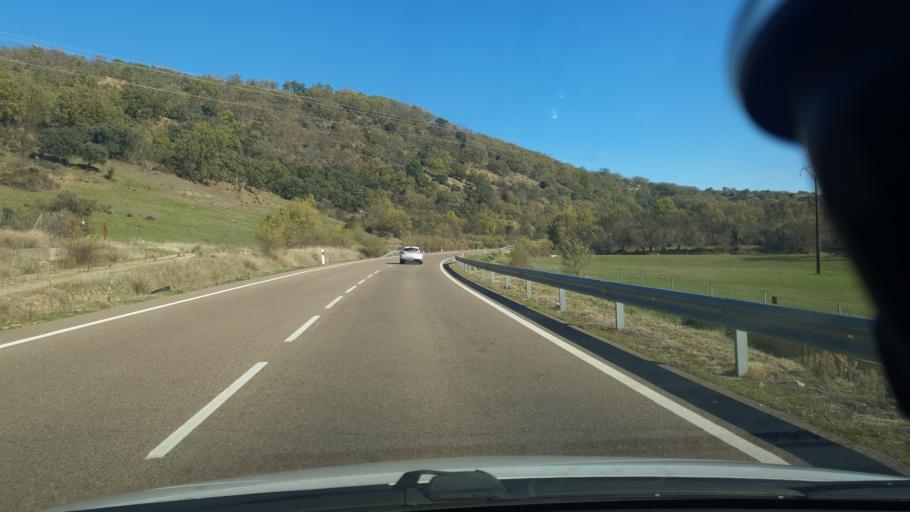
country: ES
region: Castille and Leon
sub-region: Provincia de Avila
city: Poyales del Hoyo
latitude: 40.1546
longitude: -5.1873
